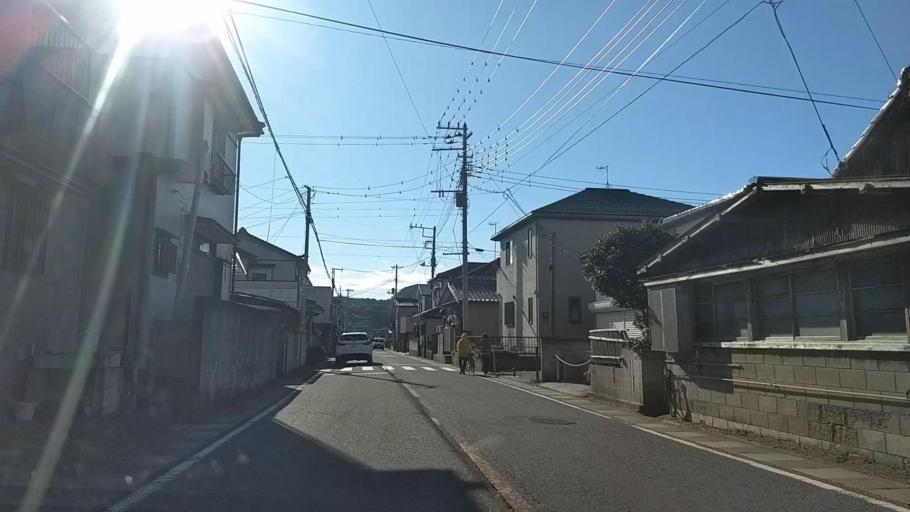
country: JP
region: Chiba
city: Tateyama
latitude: 35.1398
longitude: 139.8370
